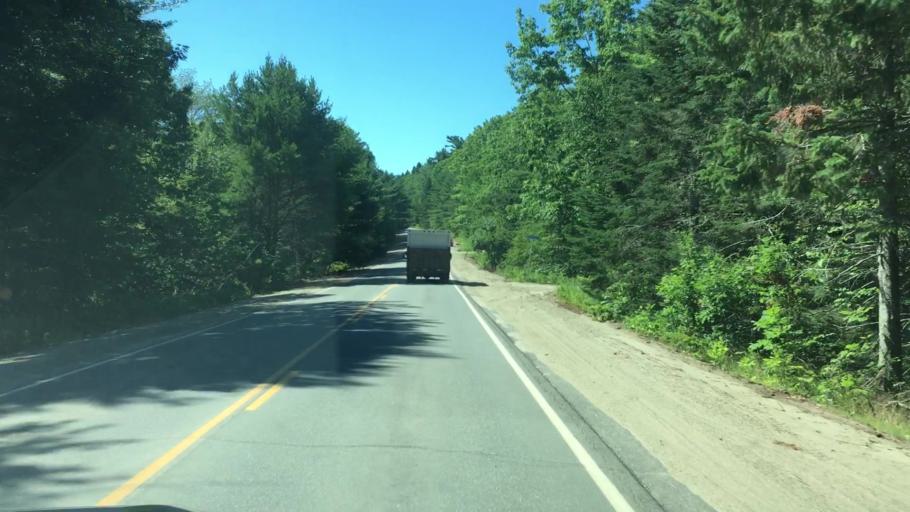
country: US
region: Maine
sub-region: Hancock County
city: Sedgwick
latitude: 44.3788
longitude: -68.5685
